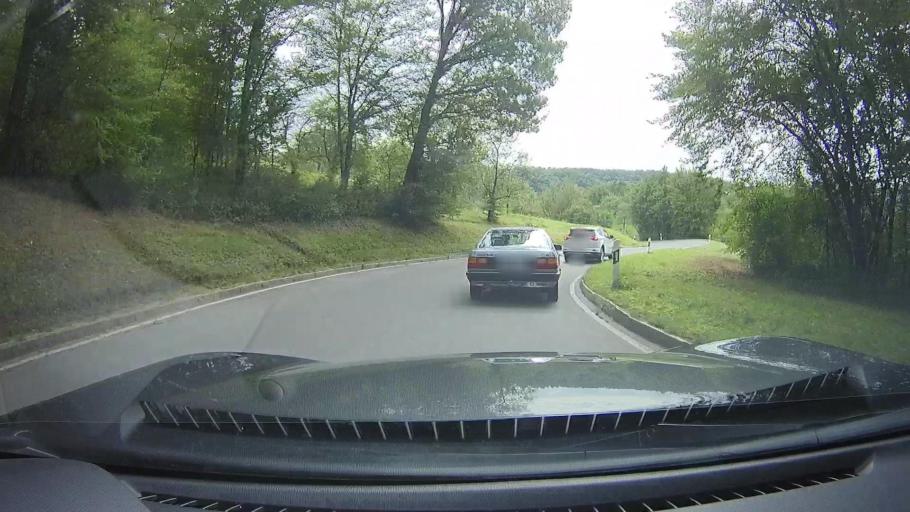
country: DE
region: Baden-Wuerttemberg
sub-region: Regierungsbezirk Stuttgart
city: Althutte
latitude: 48.8990
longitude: 9.5539
